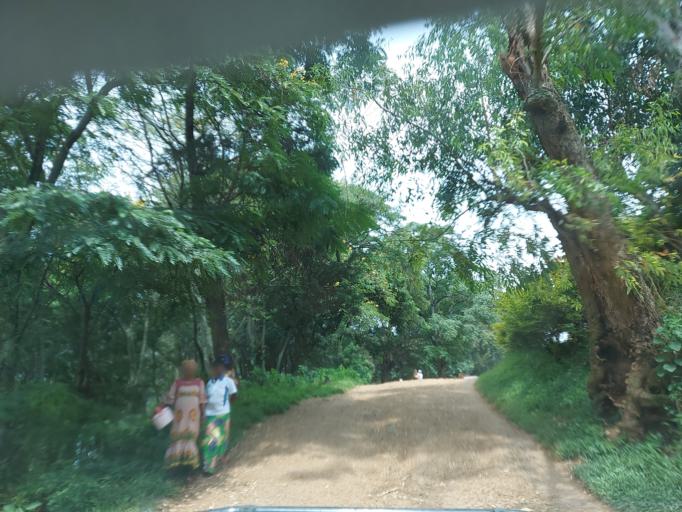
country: RW
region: Western Province
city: Cyangugu
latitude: -2.2341
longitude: 28.8591
